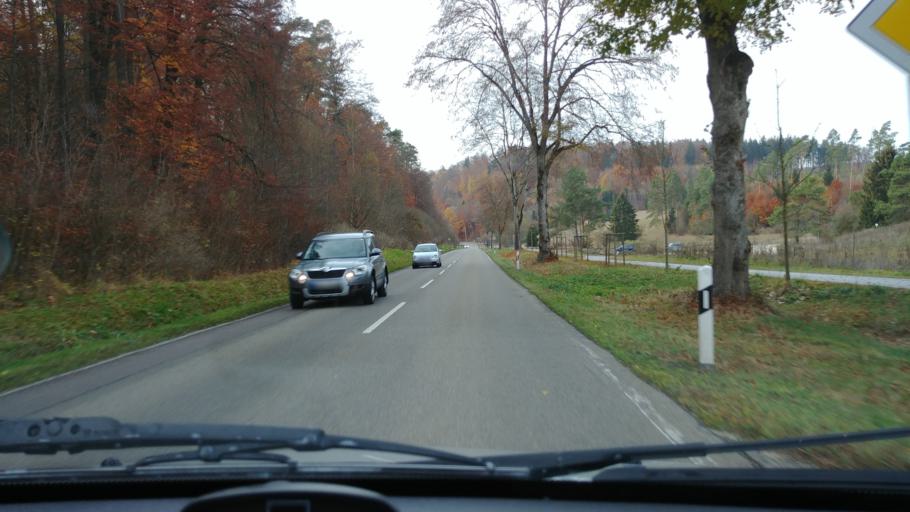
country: DE
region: Baden-Wuerttemberg
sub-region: Regierungsbezirk Stuttgart
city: Herbrechtingen
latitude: 48.6654
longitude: 10.2006
